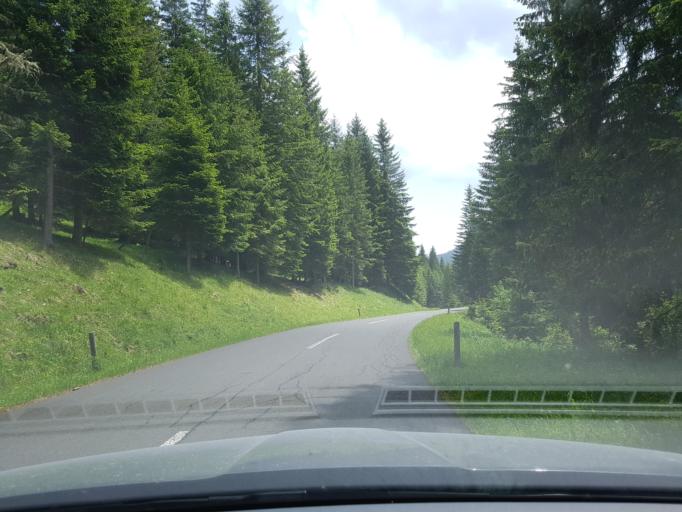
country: AT
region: Carinthia
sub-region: Politischer Bezirk Spittal an der Drau
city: Kleinkirchheim
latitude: 46.8897
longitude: 13.8405
